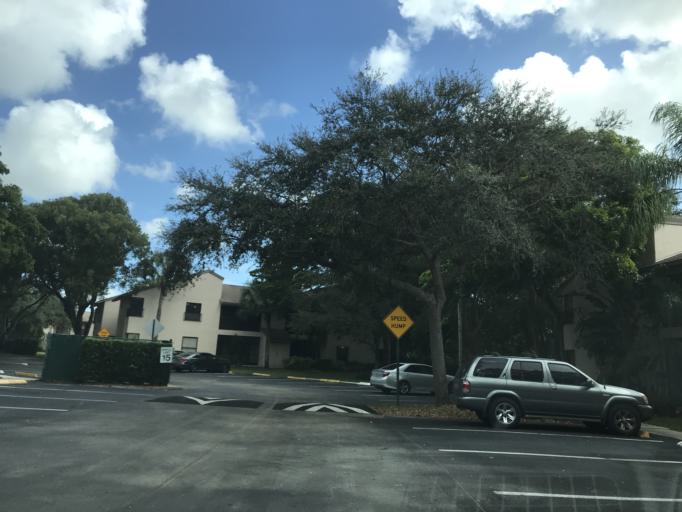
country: US
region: Florida
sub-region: Broward County
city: Coconut Creek
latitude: 26.2674
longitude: -80.1879
